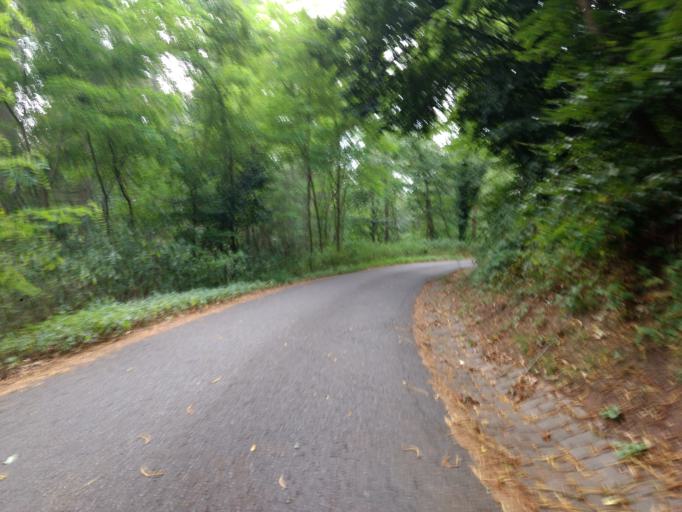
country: DE
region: Saarland
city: Wallerfangen
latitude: 49.3335
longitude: 6.6976
